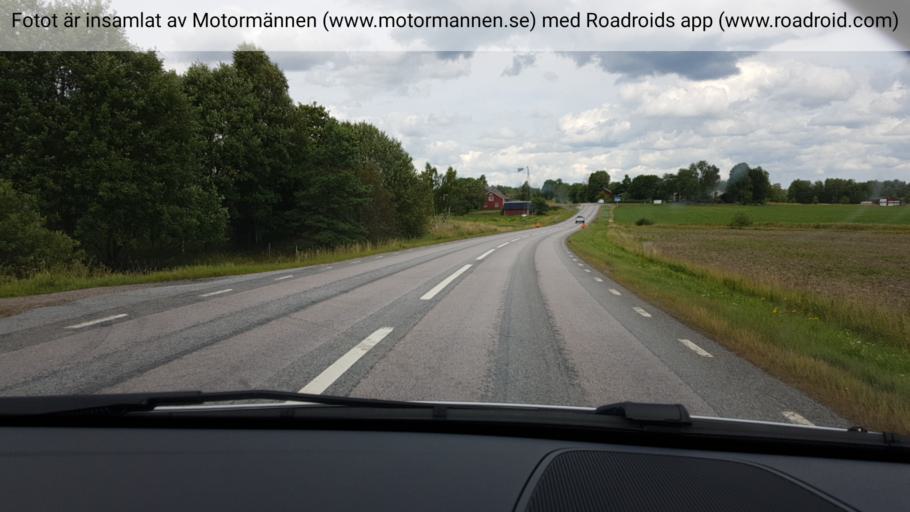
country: SE
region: Uppsala
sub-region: Osthammars Kommun
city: Gimo
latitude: 59.9483
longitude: 18.1156
